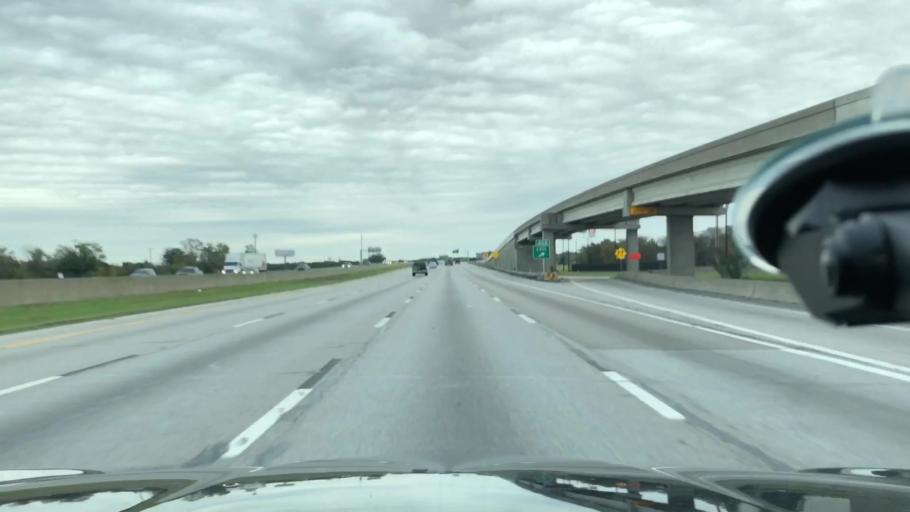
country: US
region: Texas
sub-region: Dallas County
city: DeSoto
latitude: 32.6421
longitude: -96.8119
